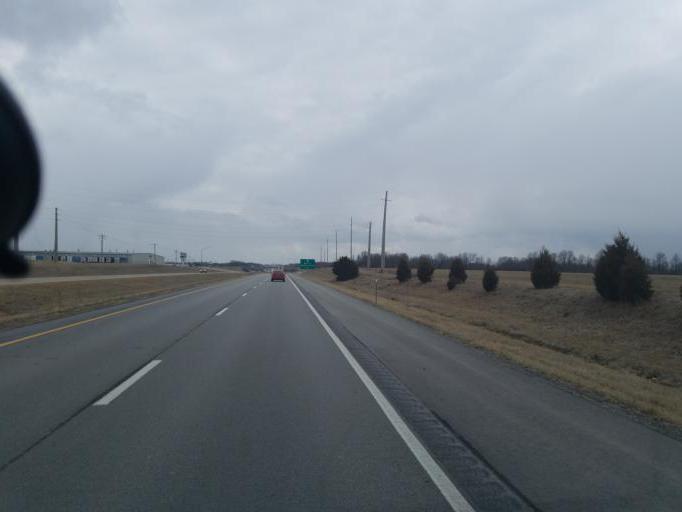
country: US
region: Missouri
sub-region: Randolph County
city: Moberly
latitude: 39.4012
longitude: -92.4128
